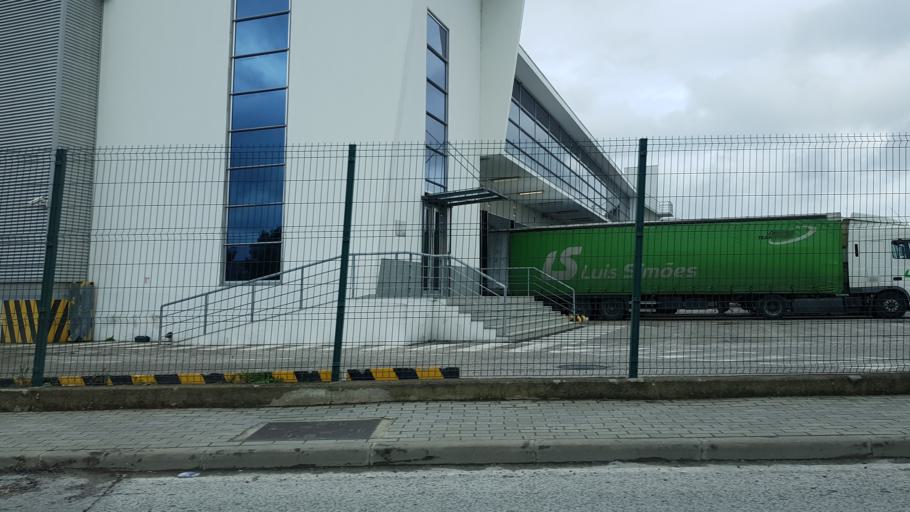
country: PT
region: Lisbon
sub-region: Alenquer
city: Carregado
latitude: 39.0313
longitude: -8.9675
